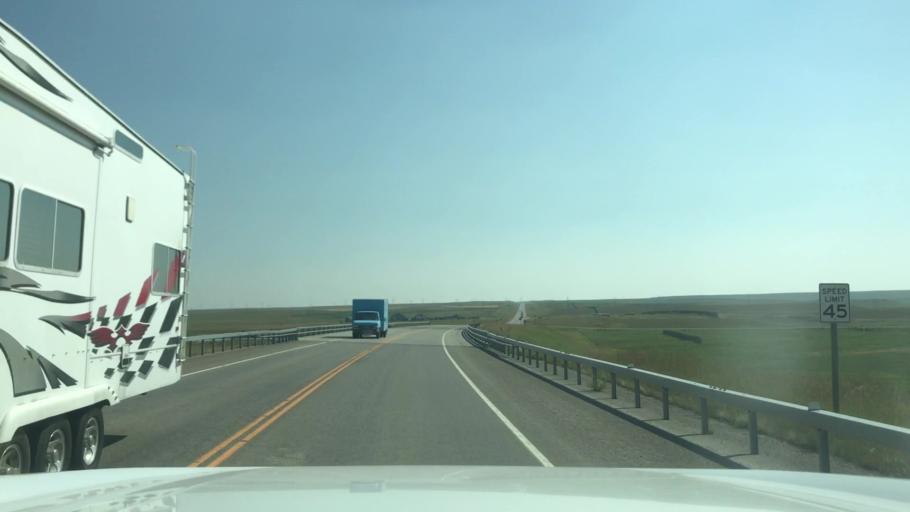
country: US
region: Montana
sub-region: Wheatland County
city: Harlowton
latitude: 46.6748
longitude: -109.7525
